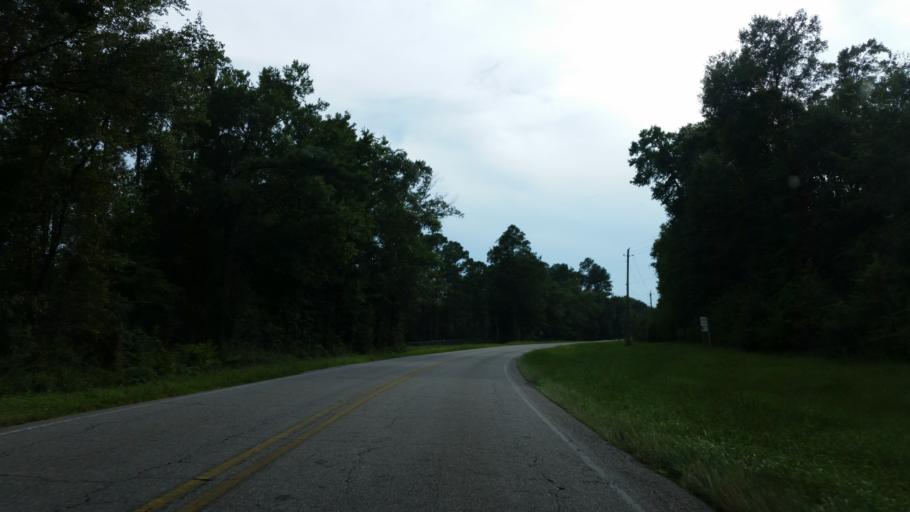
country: US
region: Florida
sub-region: Santa Rosa County
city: Milton
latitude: 30.6437
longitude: -87.0175
